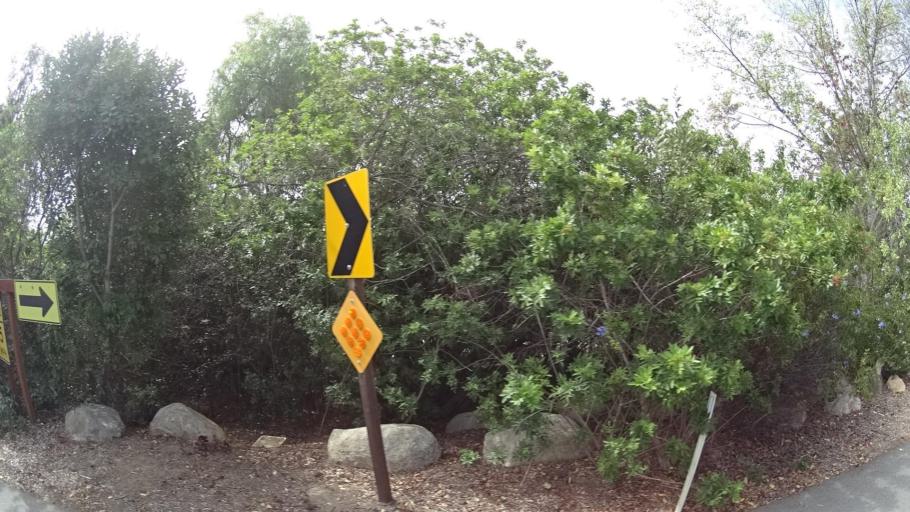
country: US
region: California
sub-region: San Diego County
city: Rancho Santa Fe
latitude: 33.0126
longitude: -117.2041
